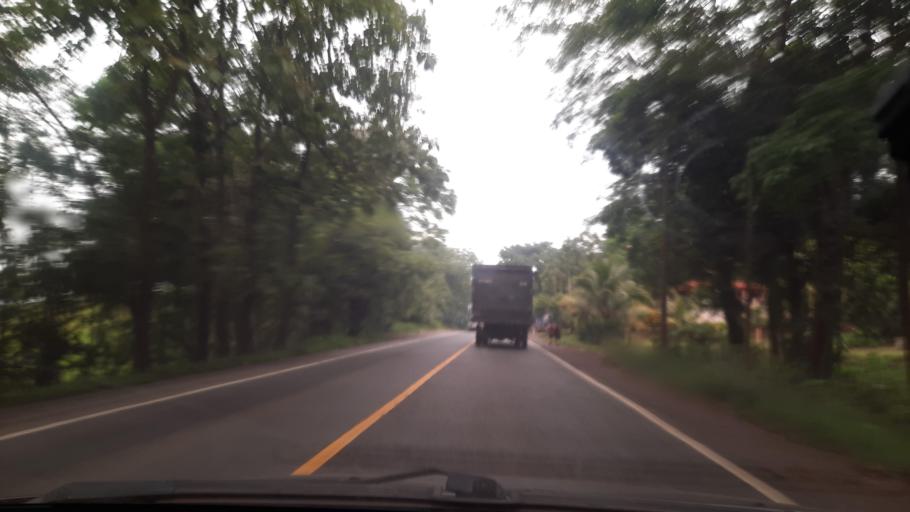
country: GT
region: Izabal
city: Morales
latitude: 15.4624
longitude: -88.9271
